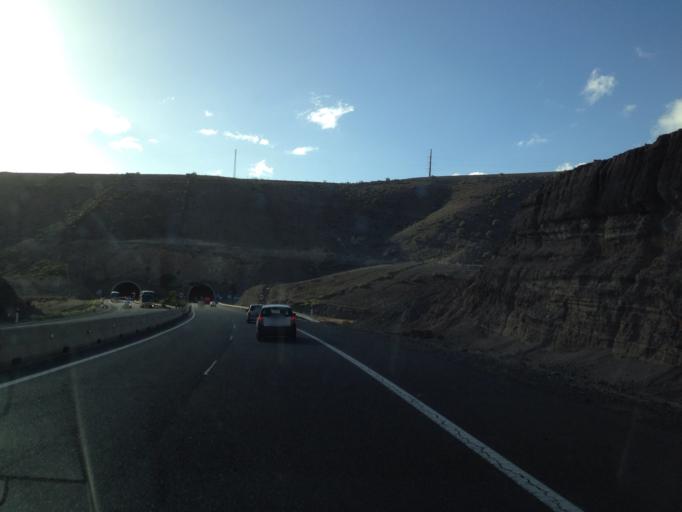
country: ES
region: Canary Islands
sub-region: Provincia de Las Palmas
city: Puerto Rico
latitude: 27.7710
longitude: -15.6551
